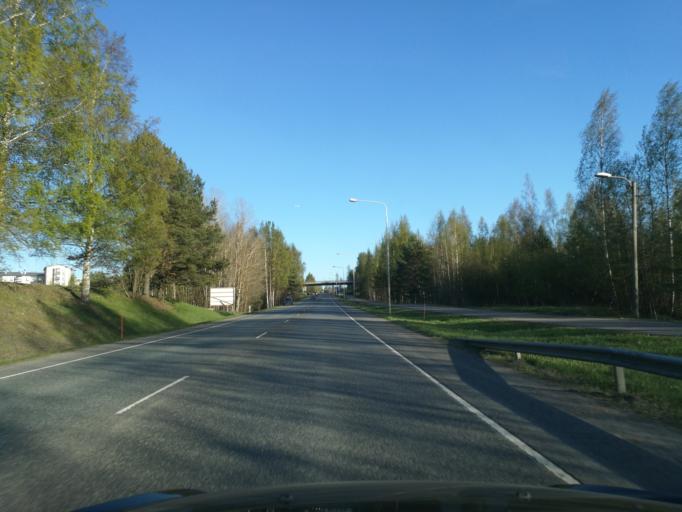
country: FI
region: Uusimaa
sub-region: Helsinki
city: Tuusula
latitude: 60.3998
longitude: 25.0144
